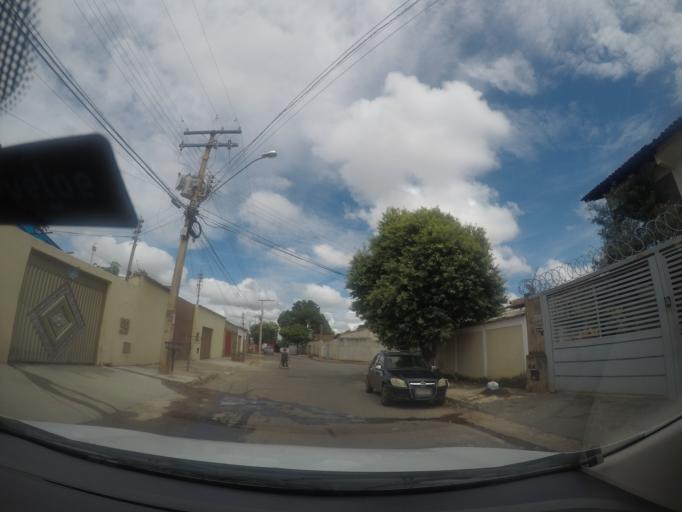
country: BR
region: Goias
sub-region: Goiania
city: Goiania
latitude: -16.6578
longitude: -49.3013
